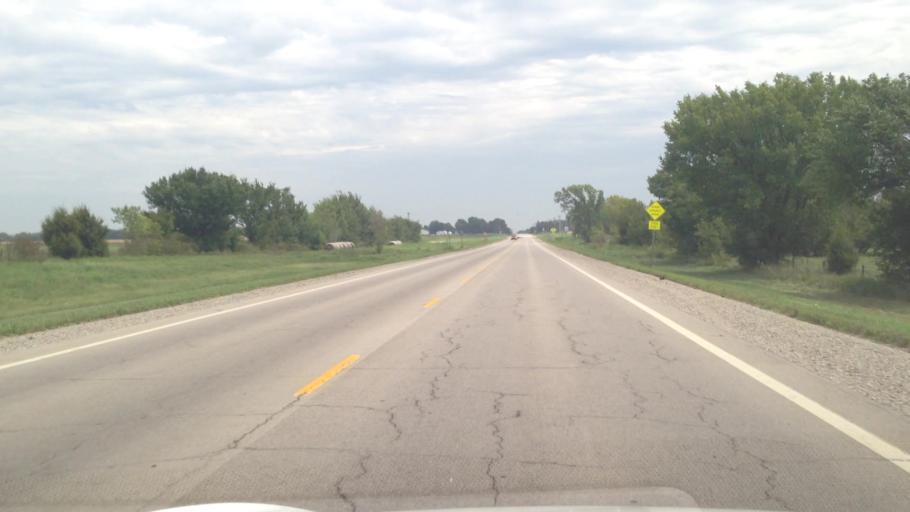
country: US
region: Kansas
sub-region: Crawford County
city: Girard
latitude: 37.5140
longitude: -94.8742
